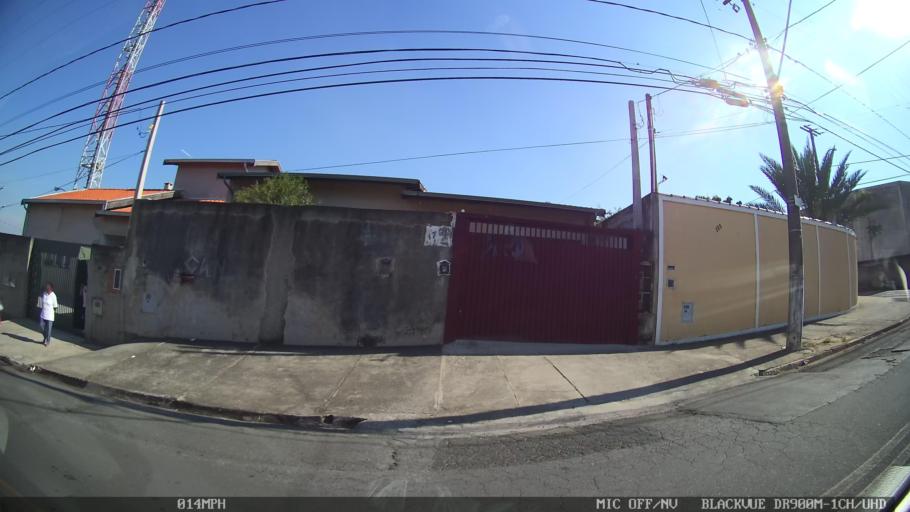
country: BR
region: Sao Paulo
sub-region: Campinas
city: Campinas
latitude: -22.9570
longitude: -47.0902
